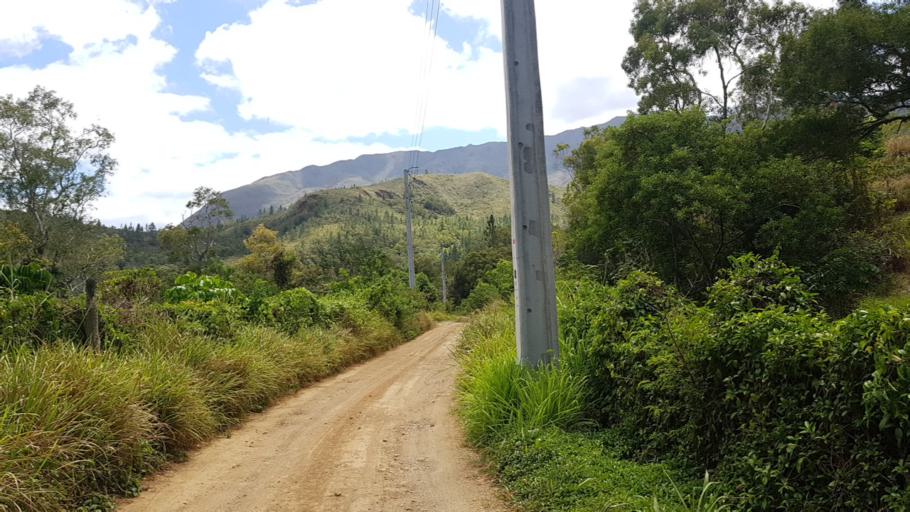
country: NC
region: South Province
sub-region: Dumbea
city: Dumbea
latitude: -22.1819
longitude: 166.4797
